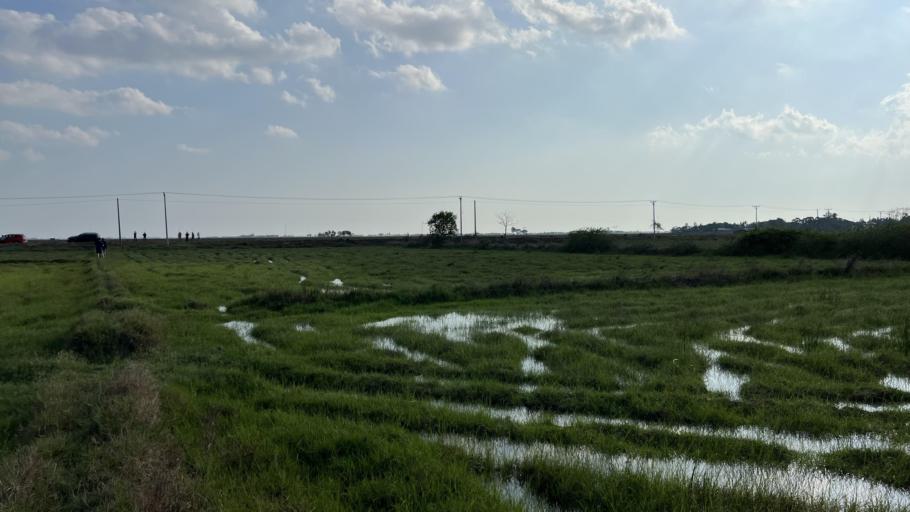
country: MM
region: Ayeyarwady
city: Pyapon
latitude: 16.1162
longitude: 95.6429
